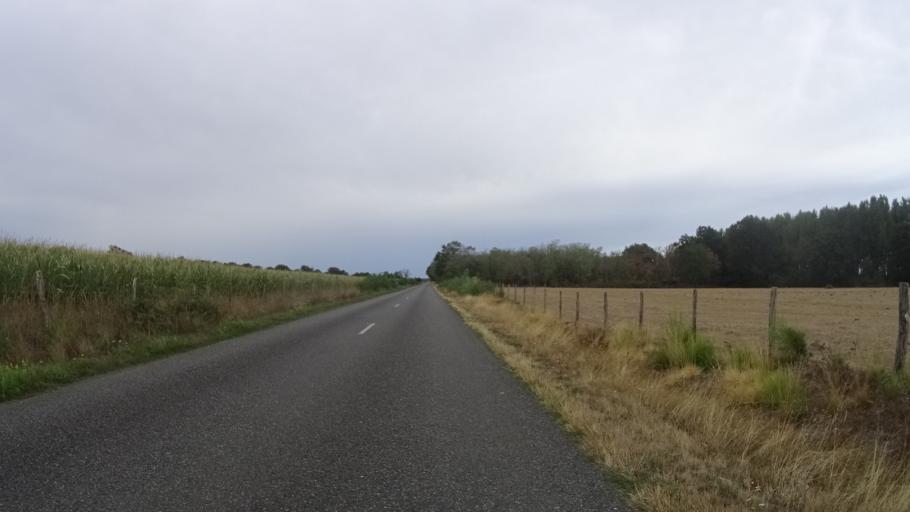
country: FR
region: Bourgogne
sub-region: Departement de la Nievre
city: Lucenay-les-Aix
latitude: 46.7682
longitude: 3.5554
